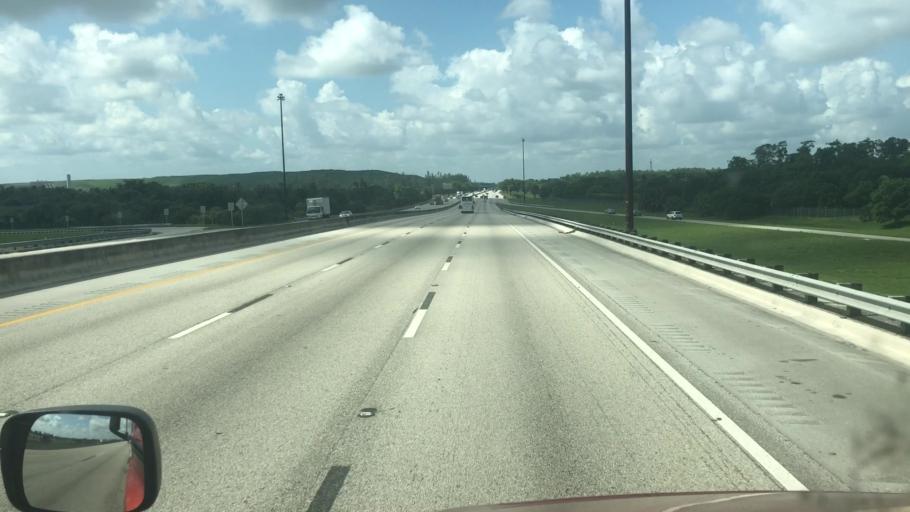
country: US
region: Florida
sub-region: Palm Beach County
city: Boca Pointe
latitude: 26.3042
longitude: -80.1697
